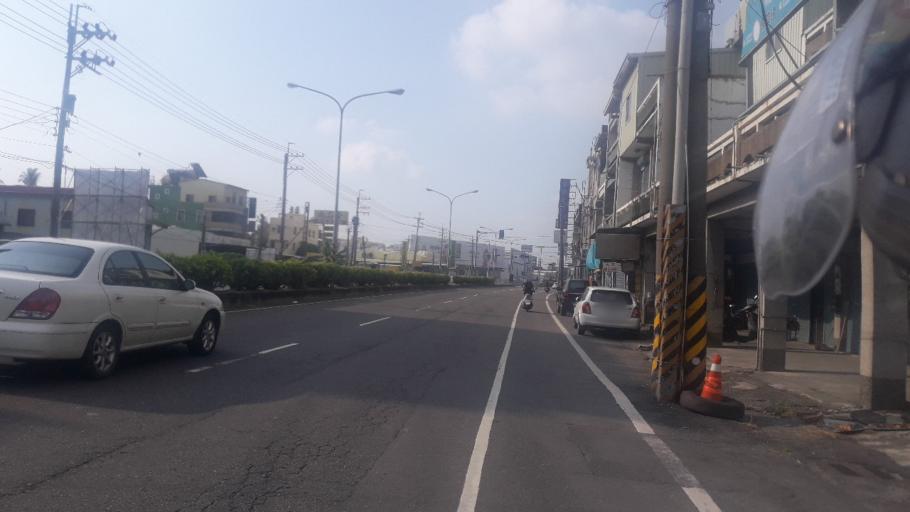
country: TW
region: Taiwan
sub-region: Tainan
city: Tainan
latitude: 22.8637
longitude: 120.2576
